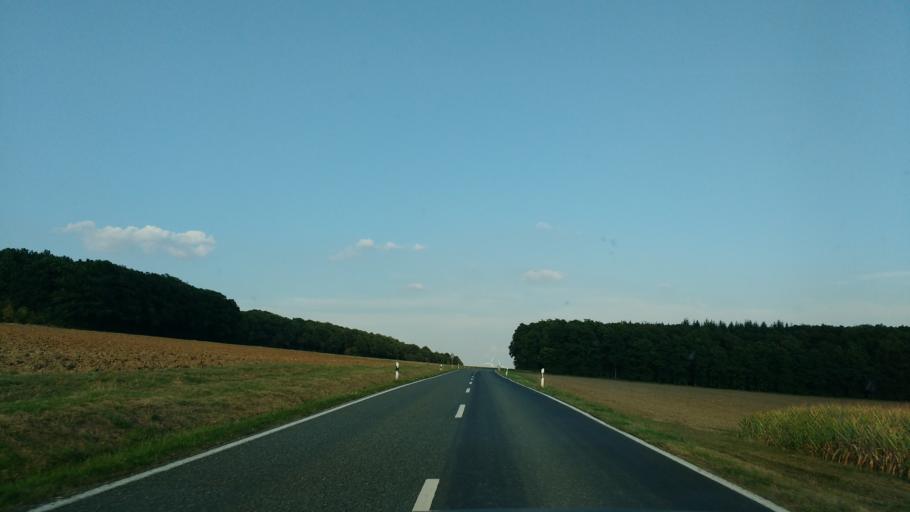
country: DE
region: Bavaria
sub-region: Regierungsbezirk Unterfranken
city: Wasserlosen
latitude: 50.0812
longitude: 10.0090
